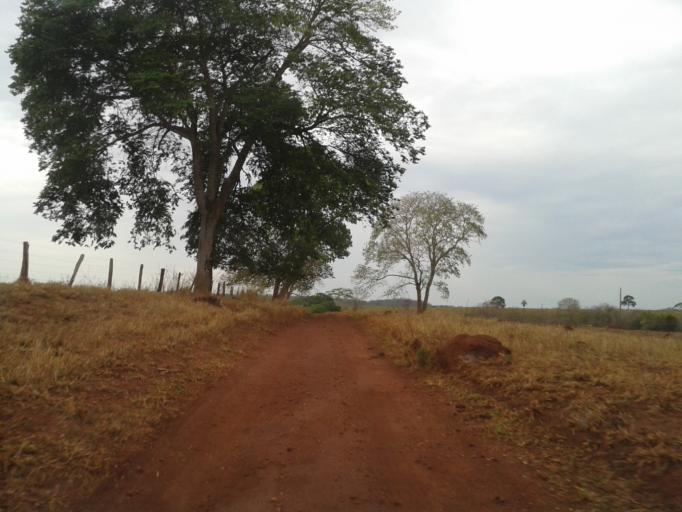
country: BR
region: Minas Gerais
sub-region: Santa Vitoria
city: Santa Vitoria
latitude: -18.8592
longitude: -49.8270
